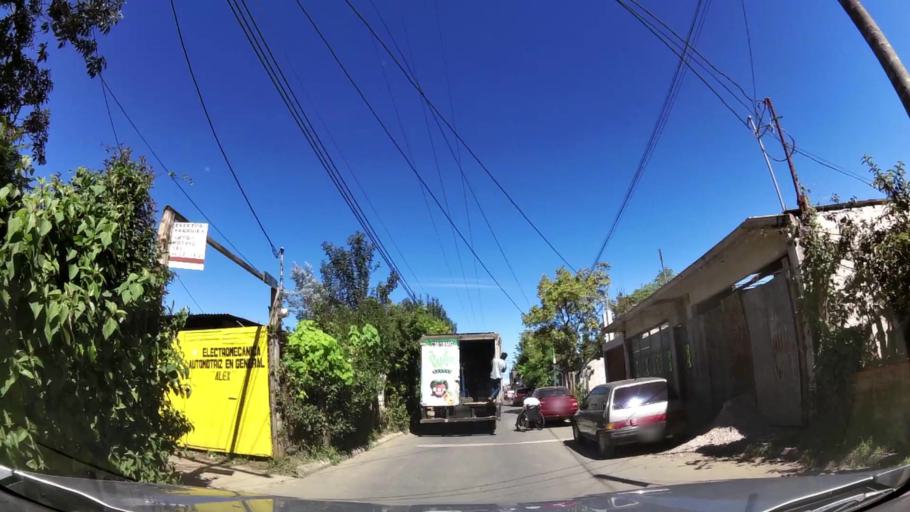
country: GT
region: Guatemala
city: San Jose Pinula
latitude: 14.5452
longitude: -90.4153
